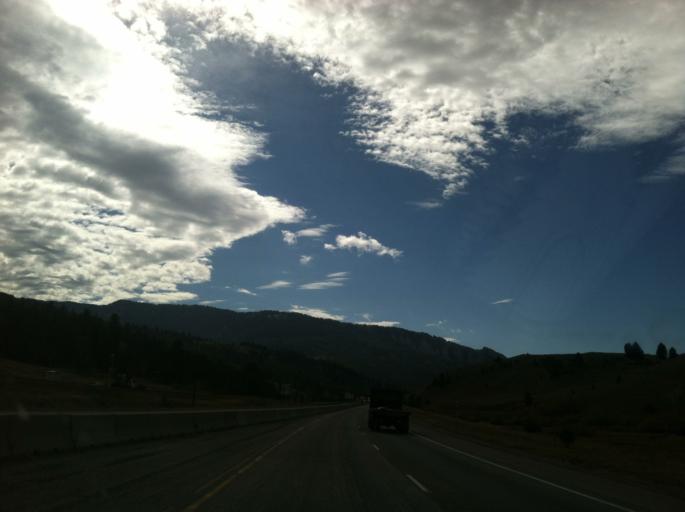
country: US
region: Montana
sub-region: Gallatin County
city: Bozeman
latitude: 45.6533
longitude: -110.8536
